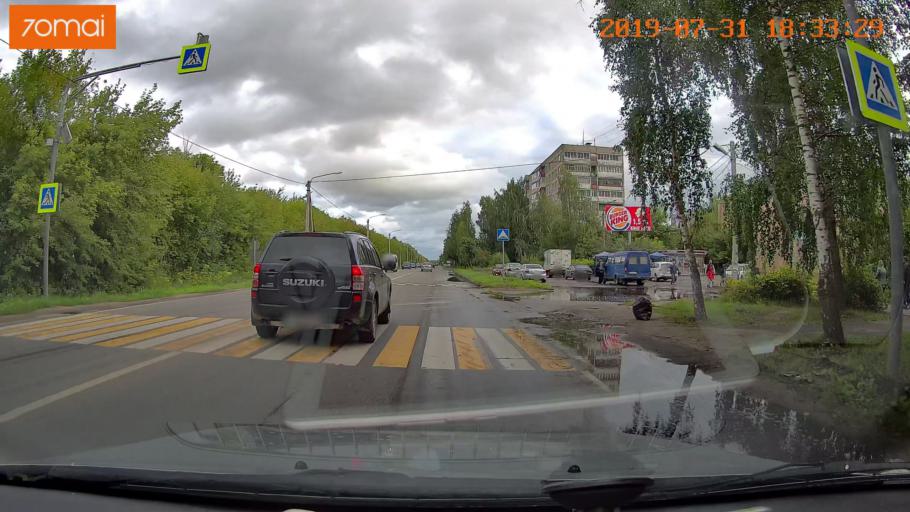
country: RU
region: Moskovskaya
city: Voskresensk
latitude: 55.3104
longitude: 38.6557
